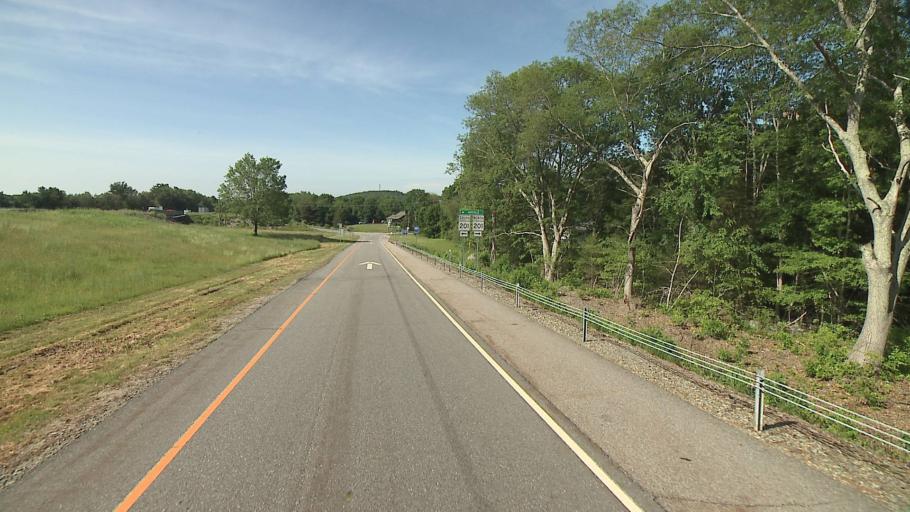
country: US
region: Connecticut
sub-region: New London County
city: Jewett City
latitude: 41.6155
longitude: -71.9462
